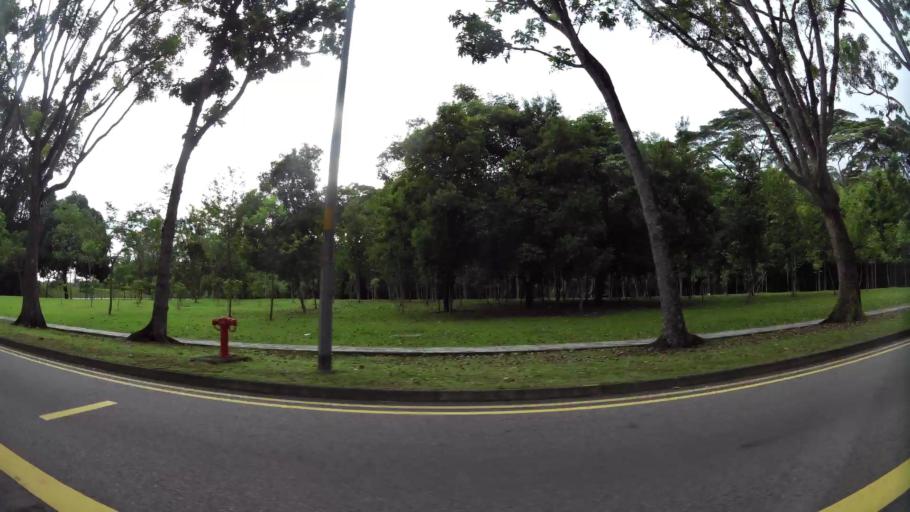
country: SG
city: Singapore
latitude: 1.3622
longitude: 103.8280
